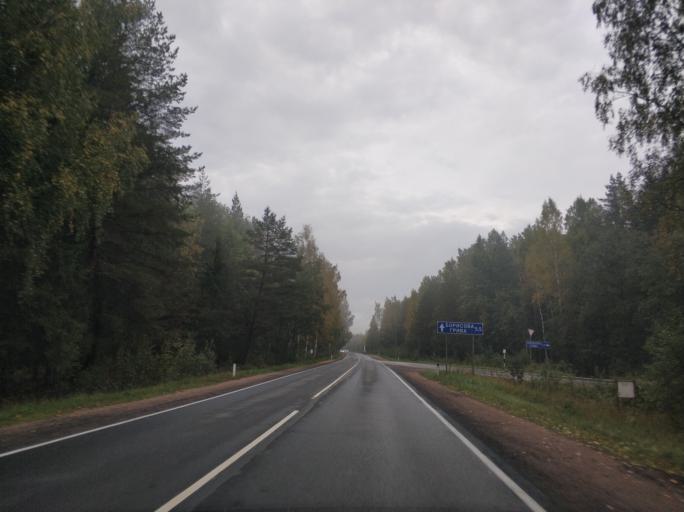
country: RU
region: Leningrad
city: Borisova Griva
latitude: 60.0903
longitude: 30.8604
